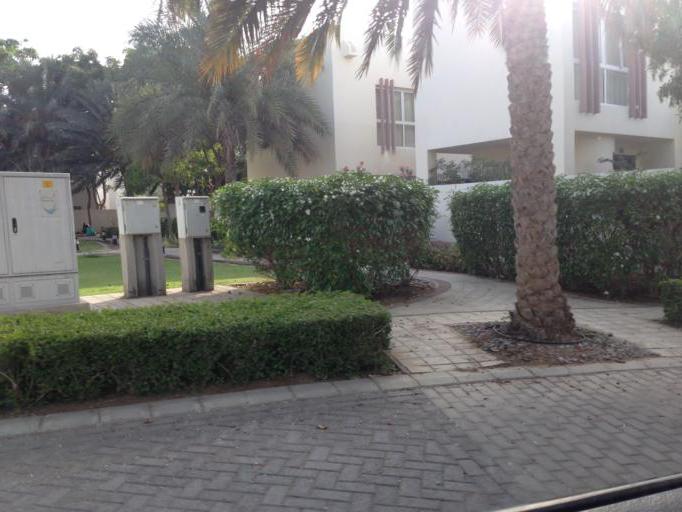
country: OM
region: Muhafazat Masqat
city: As Sib al Jadidah
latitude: 23.6234
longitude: 58.2716
